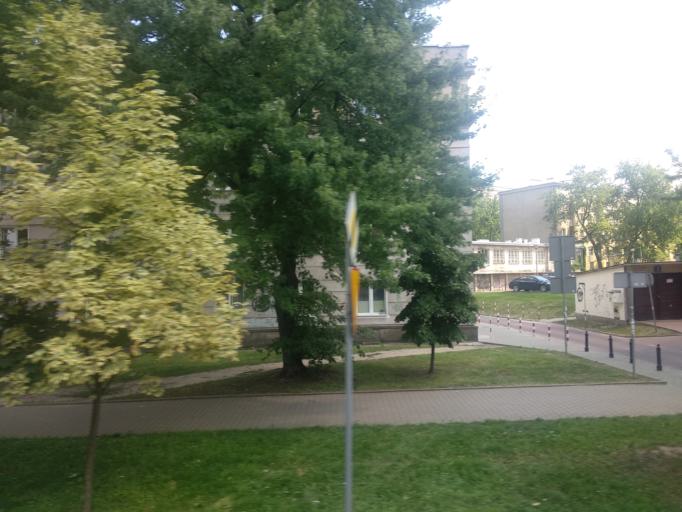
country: PL
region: Masovian Voivodeship
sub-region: Warszawa
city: Wola
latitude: 52.2530
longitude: 20.9957
